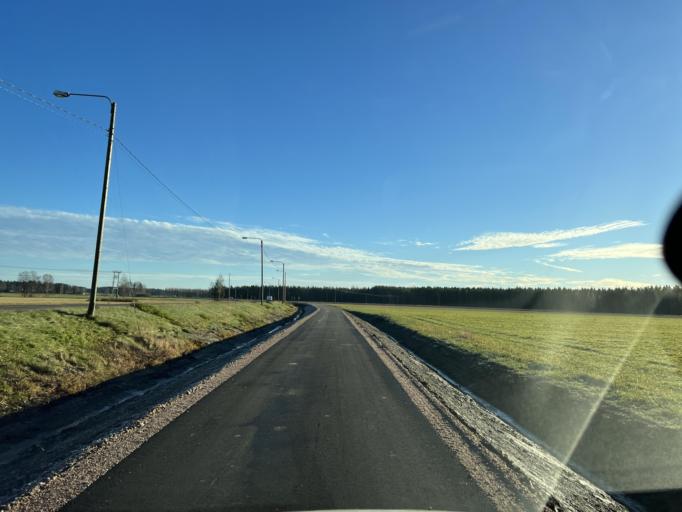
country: FI
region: Northern Ostrobothnia
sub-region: Nivala-Haapajaervi
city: Nivala
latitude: 63.9524
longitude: 24.8744
